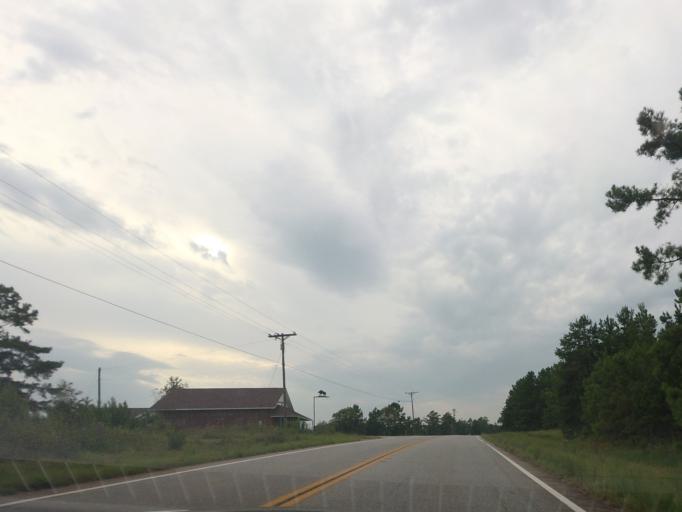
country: US
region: Georgia
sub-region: Twiggs County
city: Jeffersonville
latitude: 32.7200
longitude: -83.4115
